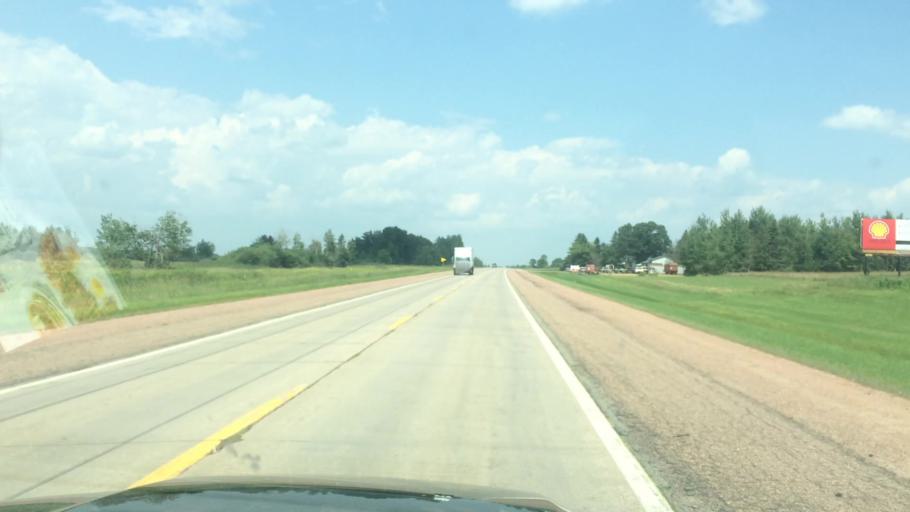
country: US
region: Wisconsin
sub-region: Clark County
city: Colby
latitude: 44.8774
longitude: -90.3157
